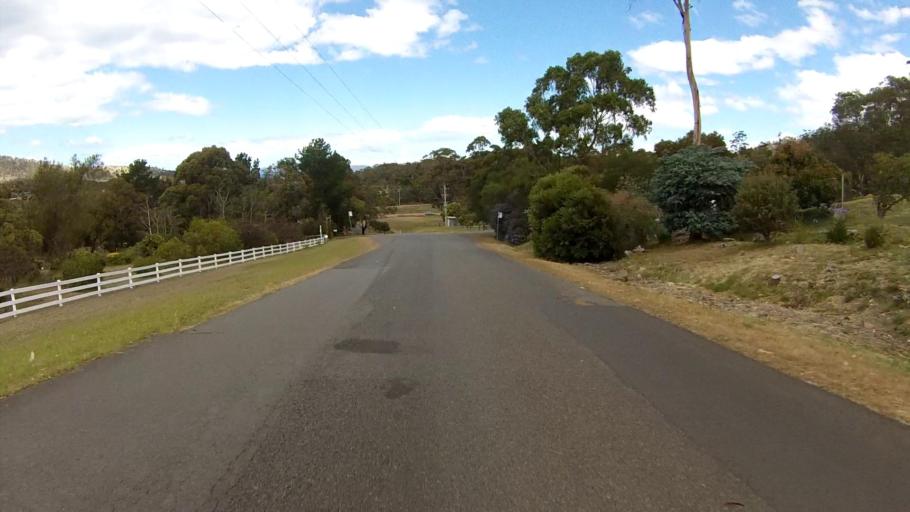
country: AU
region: Tasmania
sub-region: Clarence
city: Acton Park
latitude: -42.8706
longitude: 147.4718
